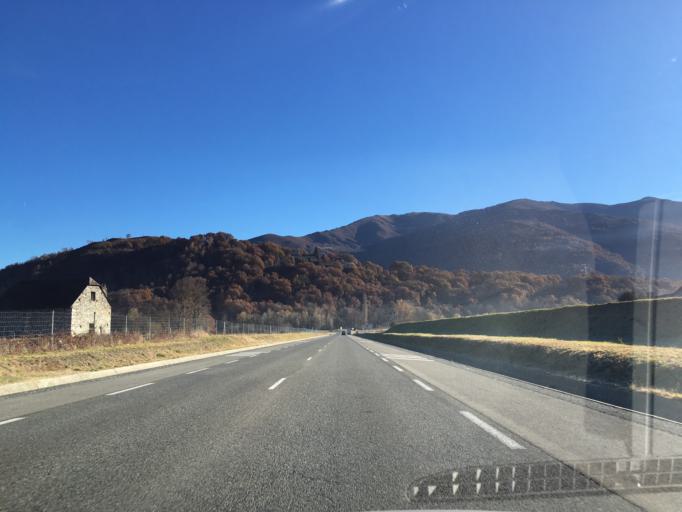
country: FR
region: Midi-Pyrenees
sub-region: Departement des Hautes-Pyrenees
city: Argeles-Gazost
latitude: 43.0123
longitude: -0.0925
